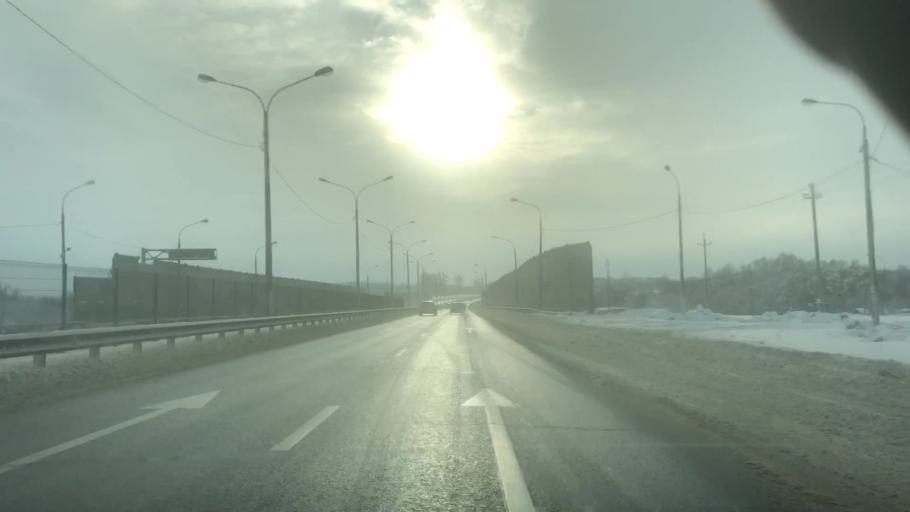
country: RU
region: Tula
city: Venev
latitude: 54.2791
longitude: 38.1599
